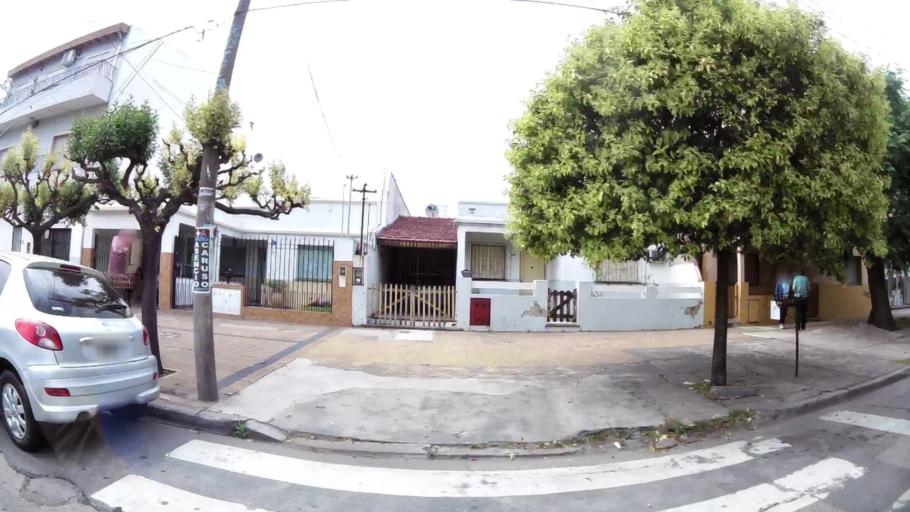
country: AR
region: Buenos Aires F.D.
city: Villa Lugano
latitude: -34.6885
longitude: -58.4962
